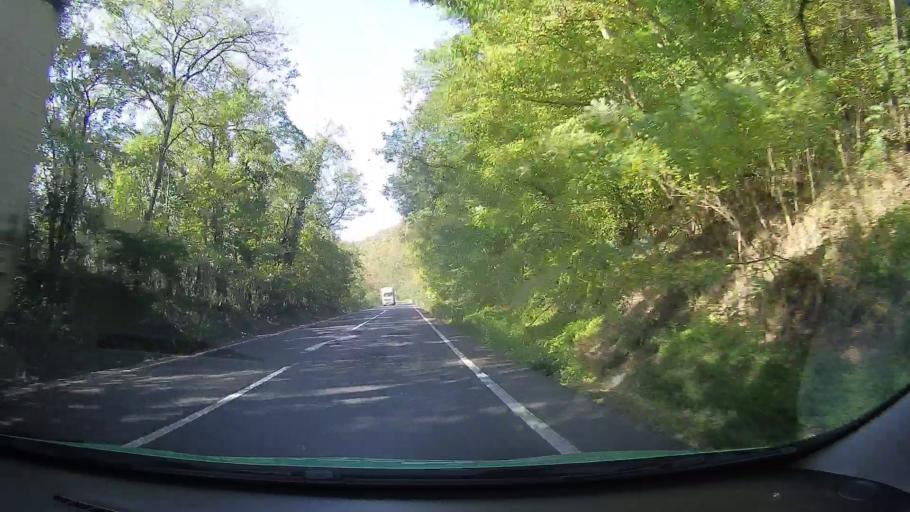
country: RO
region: Arad
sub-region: Comuna Savarsin
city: Savarsin
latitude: 46.0152
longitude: 22.2559
